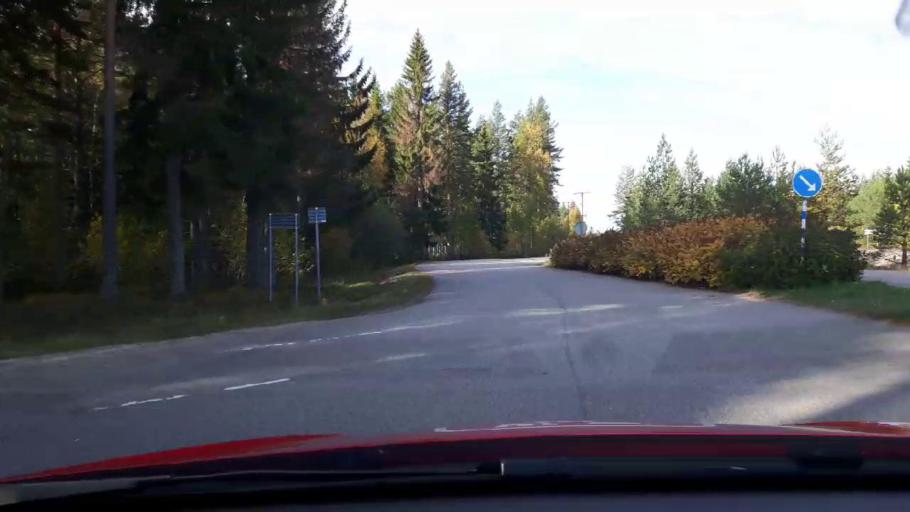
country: SE
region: Gaevleborg
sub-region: Ljusdals Kommun
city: Farila
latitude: 61.9290
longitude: 15.5534
